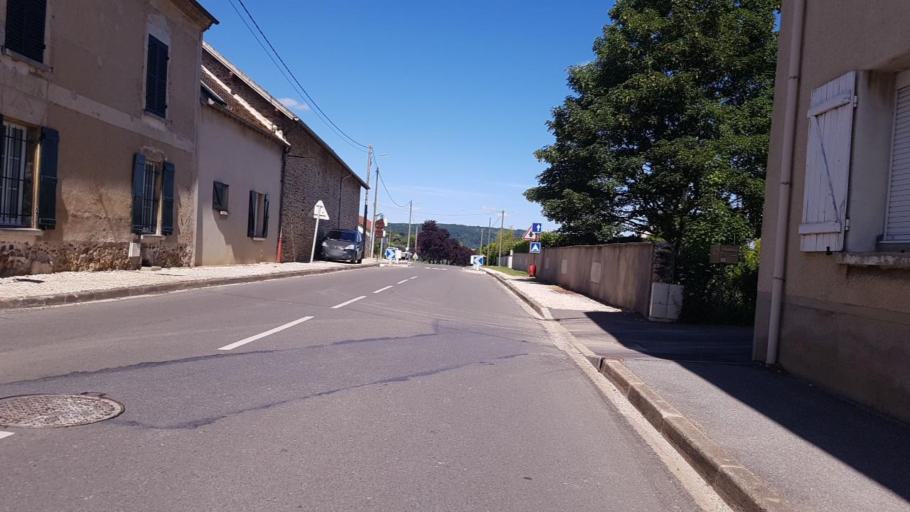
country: FR
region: Ile-de-France
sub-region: Departement de Seine-et-Marne
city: Saacy-sur-Marne
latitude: 48.9661
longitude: 3.1988
